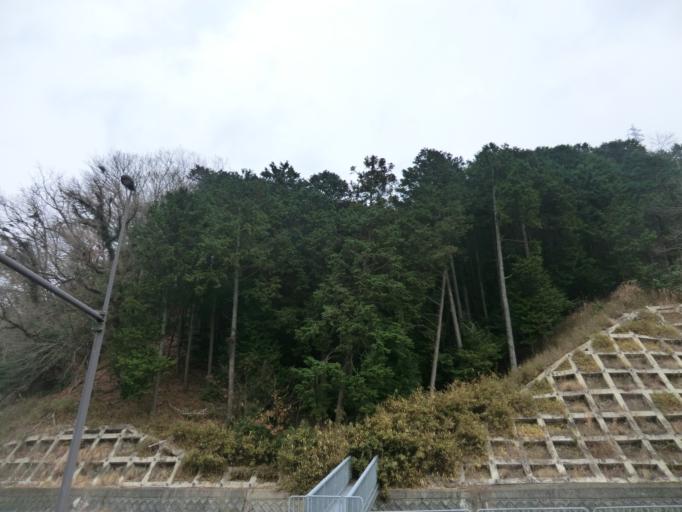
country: JP
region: Hyogo
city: Toyooka
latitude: 35.3760
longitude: 134.7859
